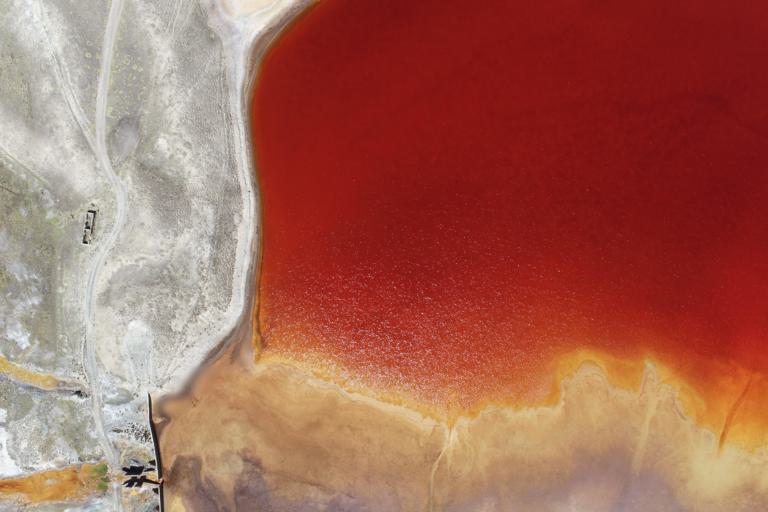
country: BO
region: La Paz
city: La Paz
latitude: -16.3421
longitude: -68.1602
